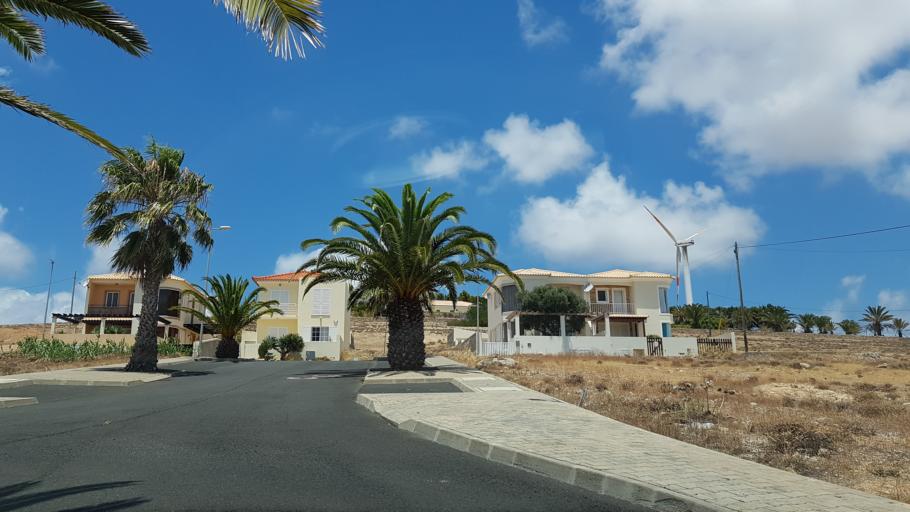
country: PT
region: Madeira
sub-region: Porto Santo
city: Vila de Porto Santo
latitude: 33.0567
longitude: -16.3622
